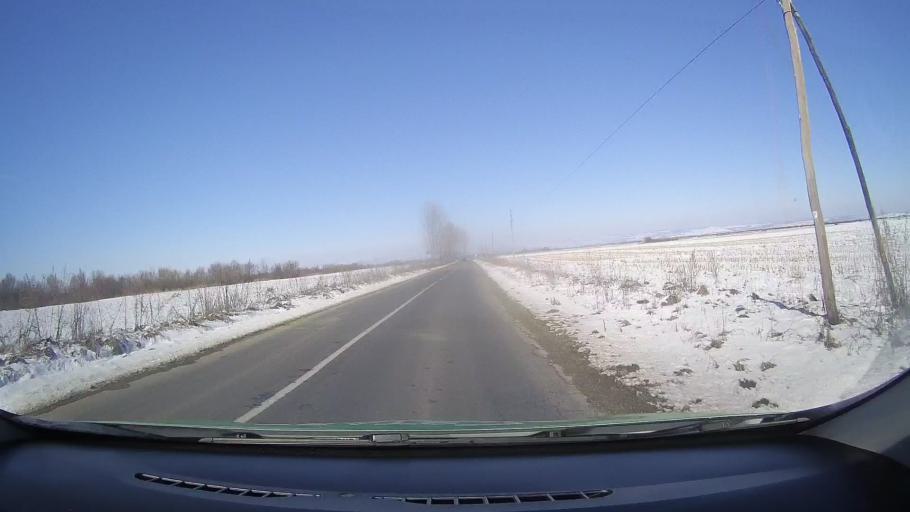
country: RO
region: Brasov
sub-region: Comuna Harseni
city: Harseni
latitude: 45.7380
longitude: 25.0219
